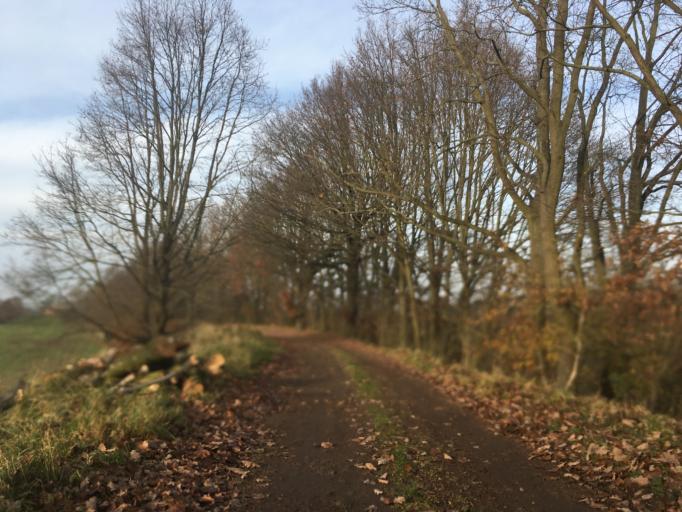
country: DE
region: Brandenburg
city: Bad Freienwalde
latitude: 52.8150
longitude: 14.0098
